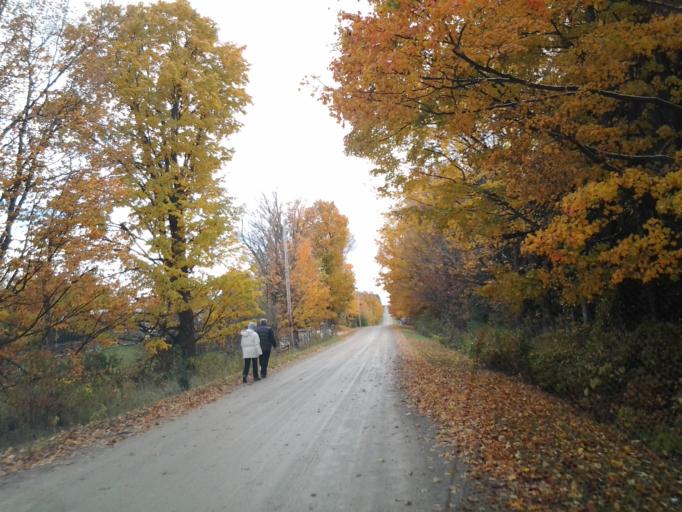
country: CA
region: Ontario
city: Shelburne
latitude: 44.0724
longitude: -80.1011
